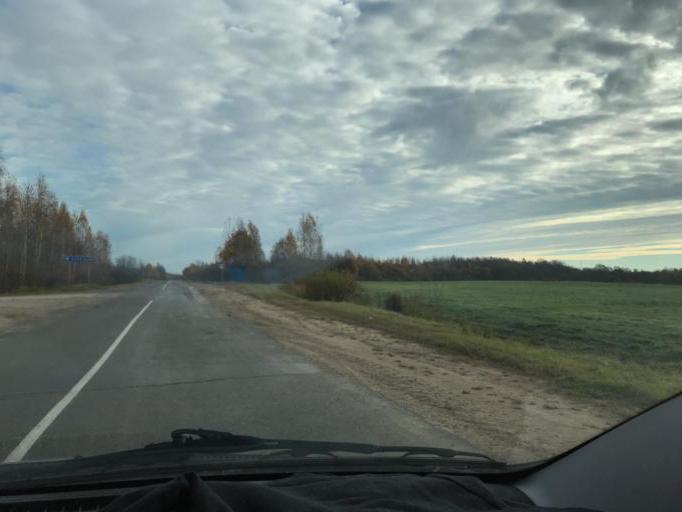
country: BY
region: Vitebsk
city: Haradok
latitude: 55.4159
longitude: 29.7732
